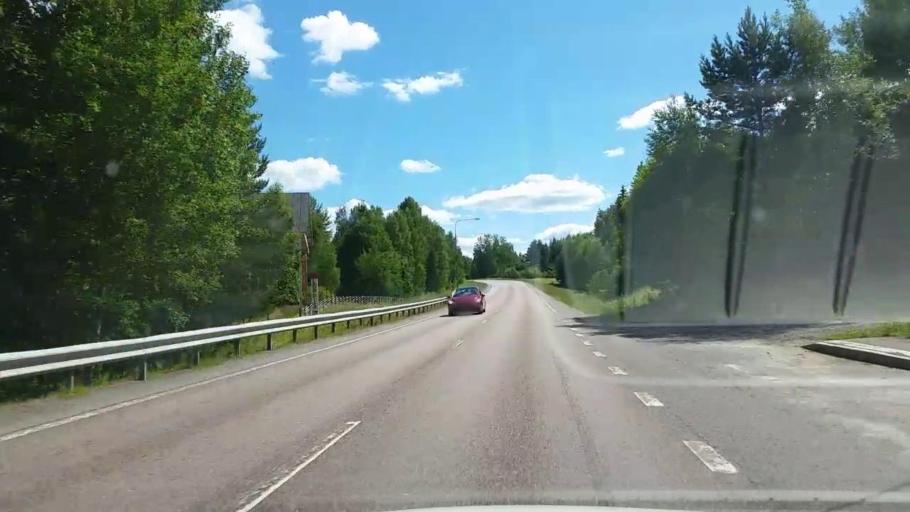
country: SE
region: Dalarna
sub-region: Faluns Kommun
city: Svardsjo
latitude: 60.8313
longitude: 15.7605
